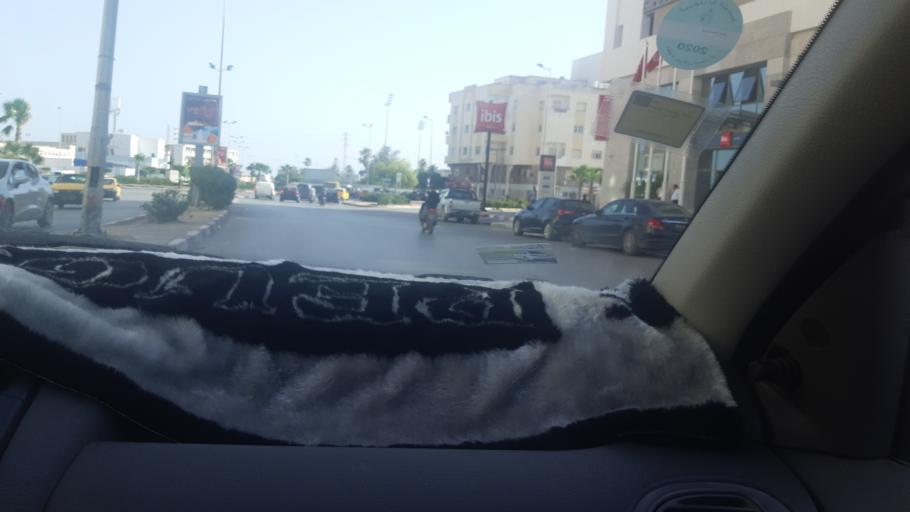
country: TN
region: Safaqis
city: Sfax
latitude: 34.7371
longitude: 10.7490
